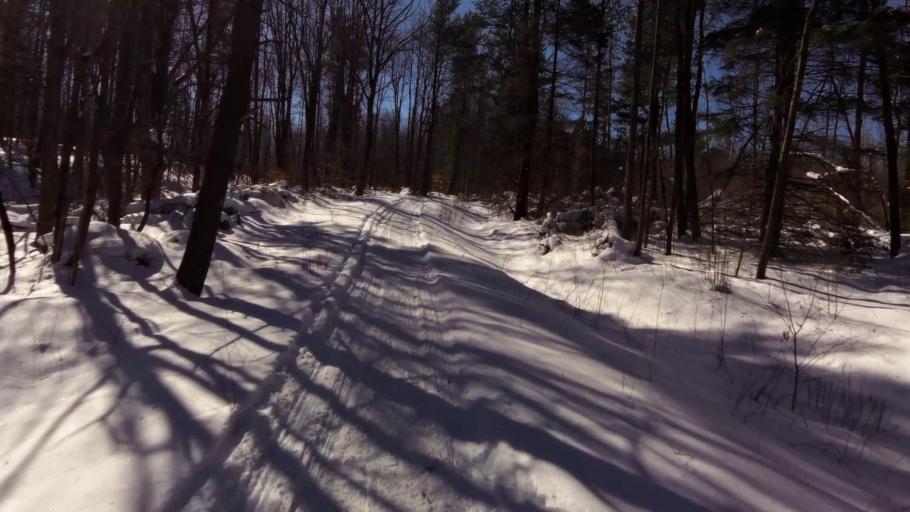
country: US
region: New York
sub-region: Allegany County
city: Cuba
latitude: 42.3034
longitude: -78.2410
